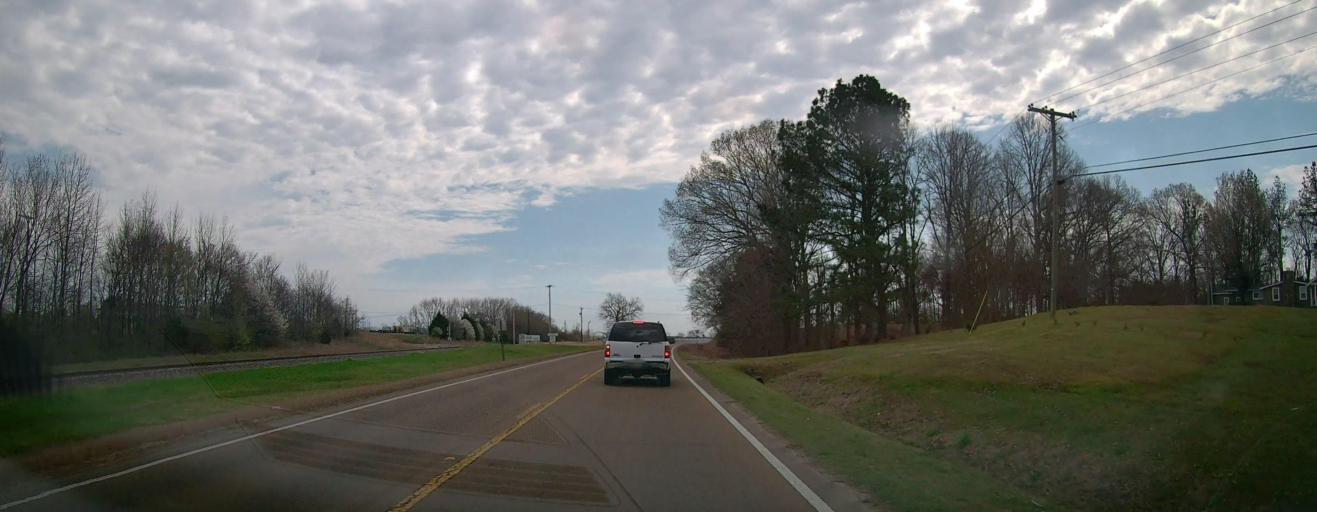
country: US
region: Mississippi
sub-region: Marshall County
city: Byhalia
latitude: 34.8691
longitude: -89.6711
